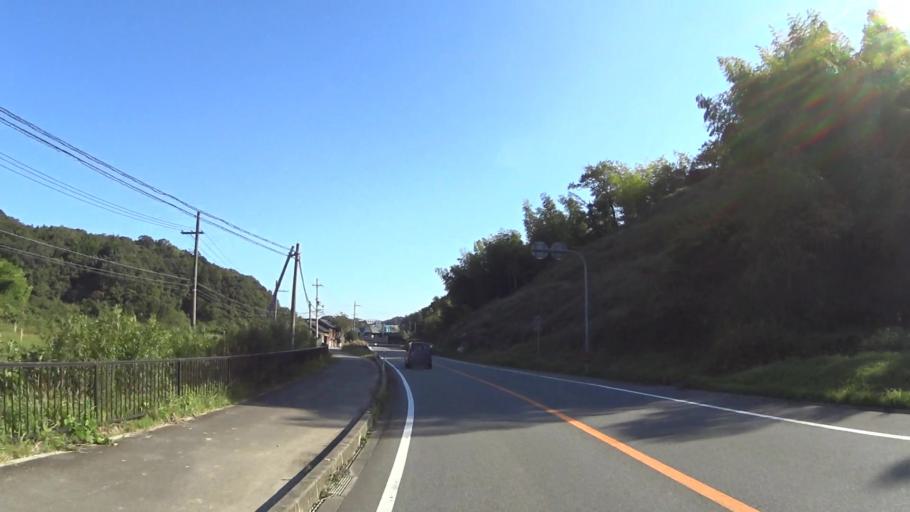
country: JP
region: Kyoto
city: Miyazu
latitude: 35.6428
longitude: 135.0515
